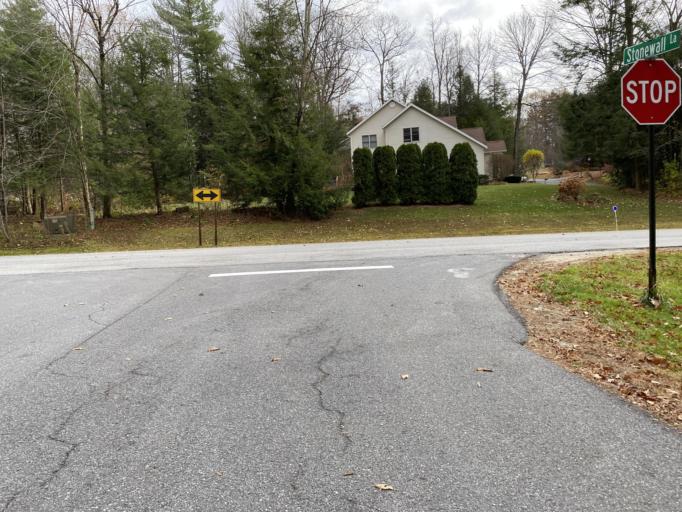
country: US
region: New York
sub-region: Saratoga County
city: Milton
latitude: 43.0957
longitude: -73.9048
